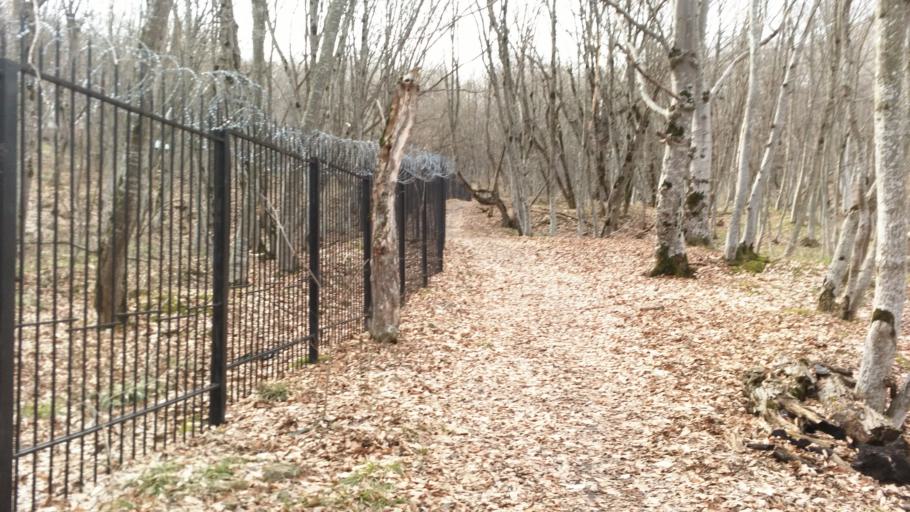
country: RU
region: Stavropol'skiy
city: Zheleznovodsk
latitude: 44.1295
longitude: 43.0246
